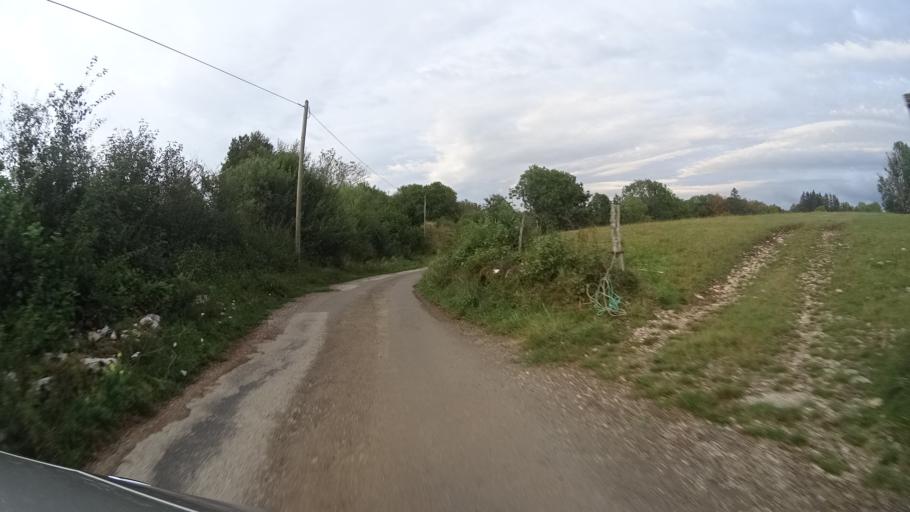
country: FR
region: Franche-Comte
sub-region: Departement du Jura
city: Morbier
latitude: 46.6171
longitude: 5.9662
